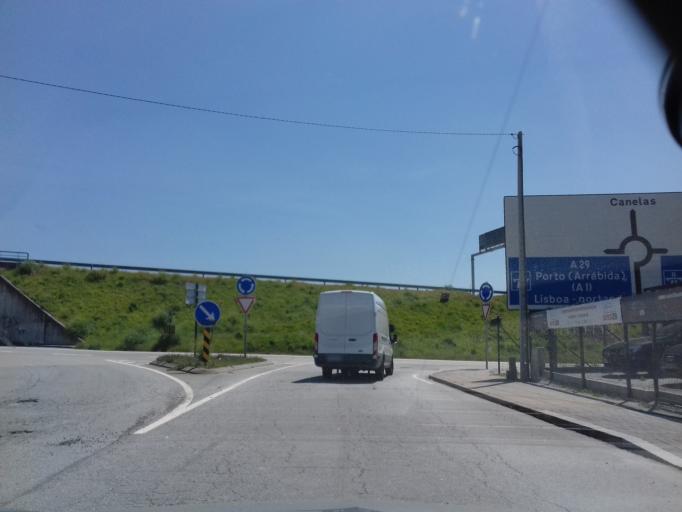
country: PT
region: Porto
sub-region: Vila Nova de Gaia
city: Canelas
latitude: 41.0893
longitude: -8.6037
